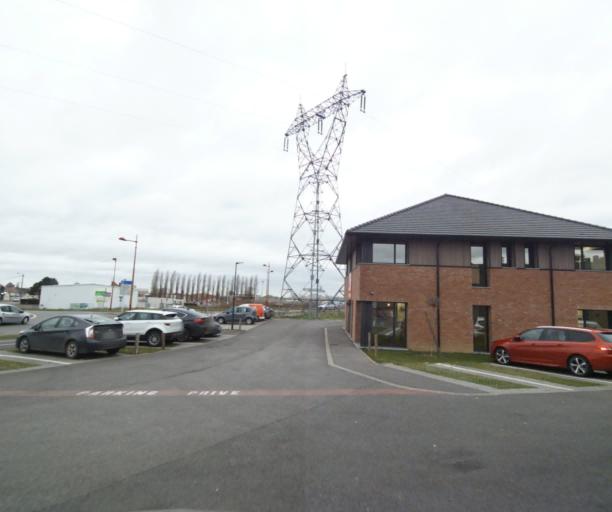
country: FR
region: Nord-Pas-de-Calais
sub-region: Departement du Nord
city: Marly
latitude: 50.3458
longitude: 3.5554
